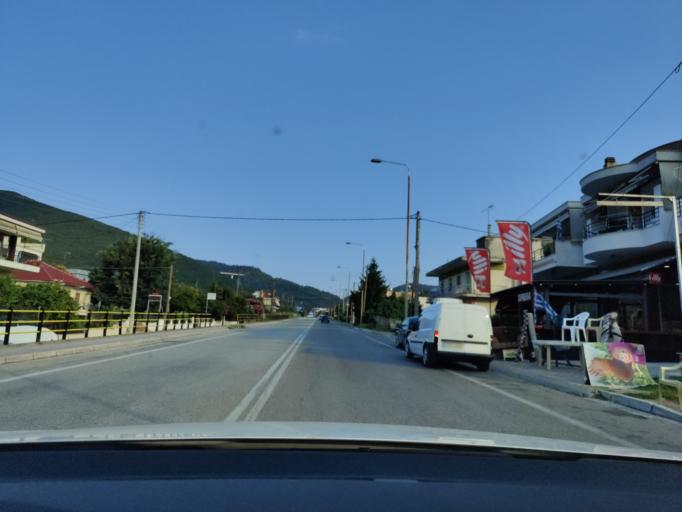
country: GR
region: East Macedonia and Thrace
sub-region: Nomos Kavalas
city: Amygdaleonas
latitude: 40.9602
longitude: 24.3616
